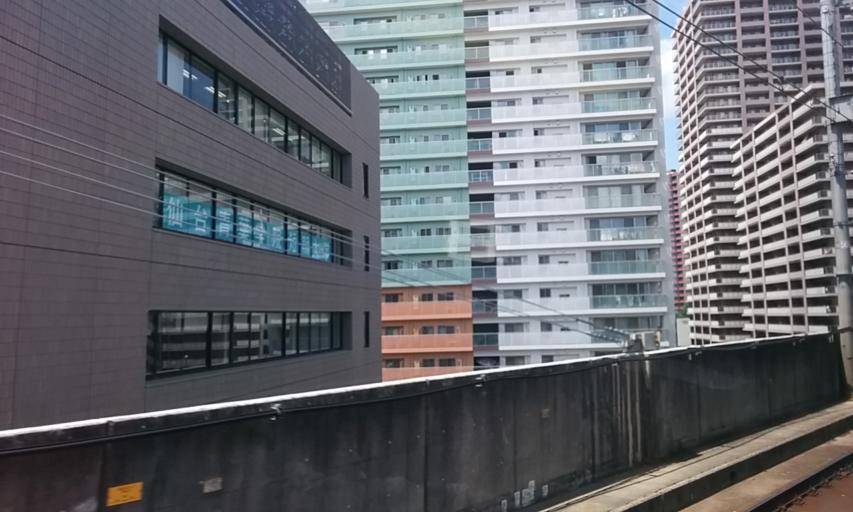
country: JP
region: Miyagi
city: Sendai
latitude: 38.2536
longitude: 140.8842
